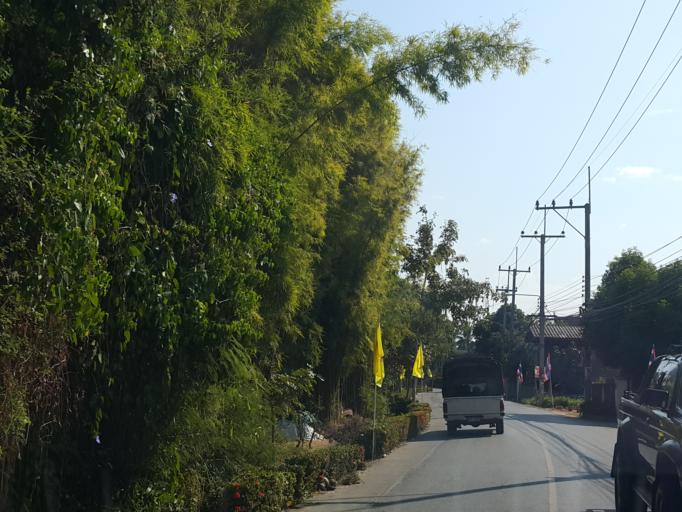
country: TH
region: Chiang Mai
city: San Sai
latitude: 18.8486
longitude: 99.0241
